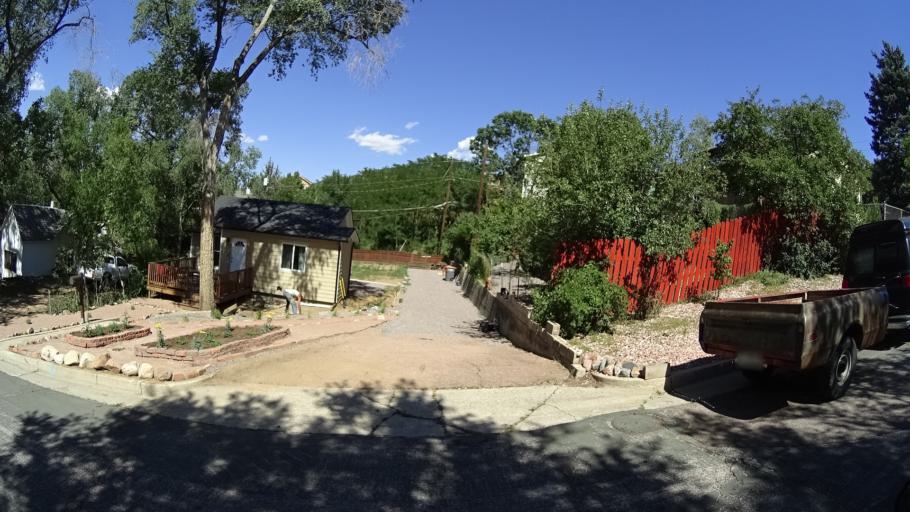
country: US
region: Colorado
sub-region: El Paso County
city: Colorado Springs
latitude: 38.8513
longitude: -104.8640
